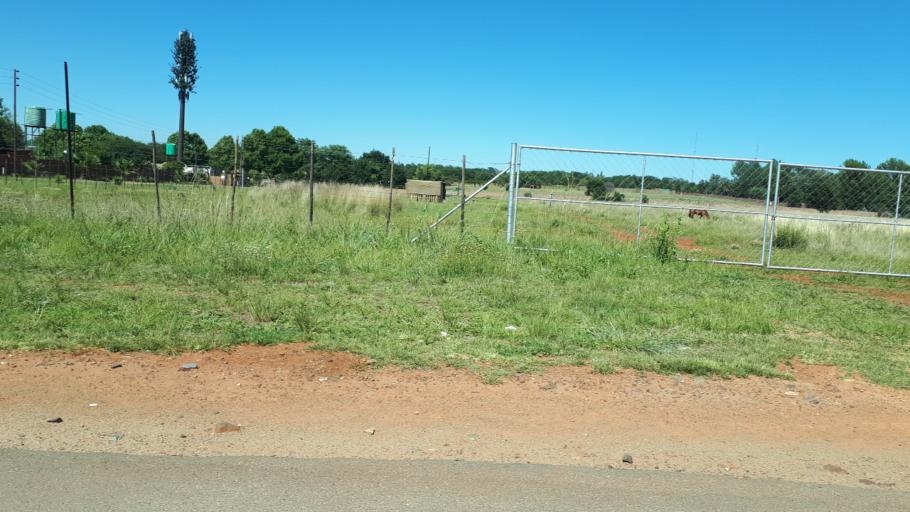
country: ZA
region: Gauteng
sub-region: City of Tshwane Metropolitan Municipality
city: Centurion
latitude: -25.8107
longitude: 28.3542
